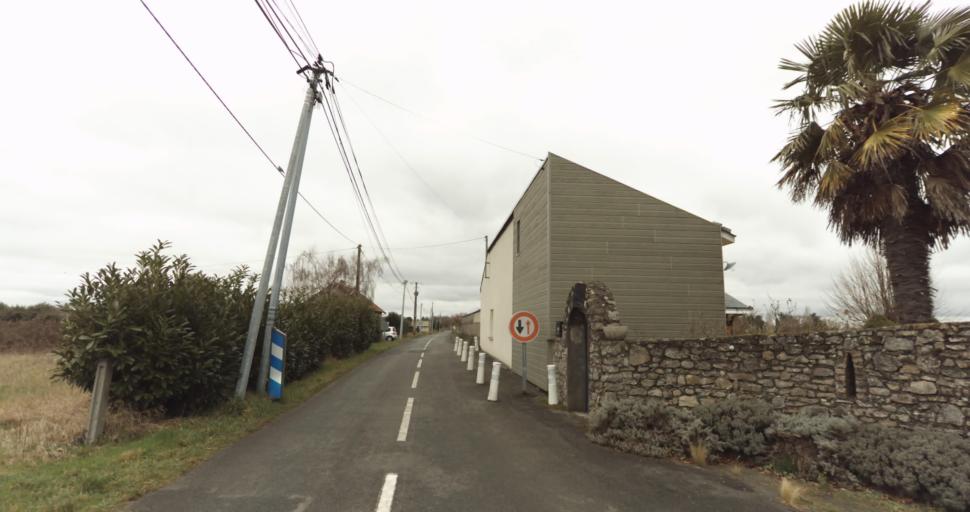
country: FR
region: Pays de la Loire
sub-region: Departement de Maine-et-Loire
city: Distre
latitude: 47.2419
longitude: -0.1056
